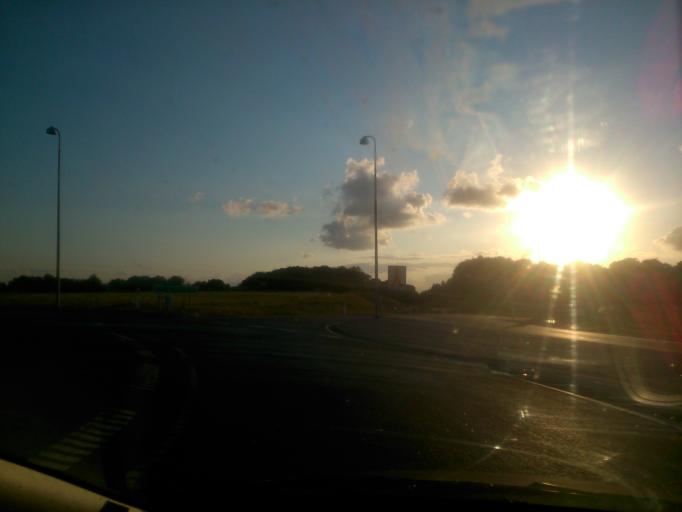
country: DK
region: South Denmark
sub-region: Middelfart Kommune
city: Strib
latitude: 55.5140
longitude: 9.7757
